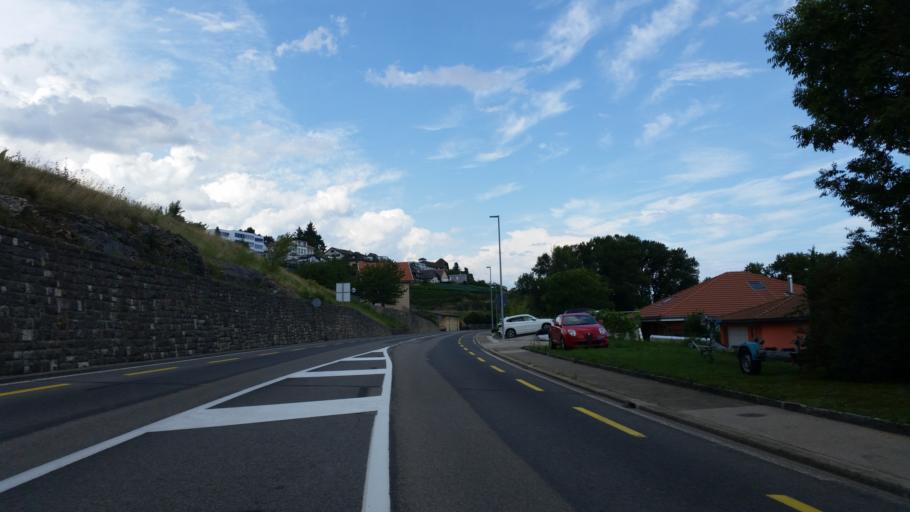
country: CH
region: Neuchatel
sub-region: Boudry District
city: Saint-Aubin-Sauges
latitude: 46.8891
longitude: 6.7673
